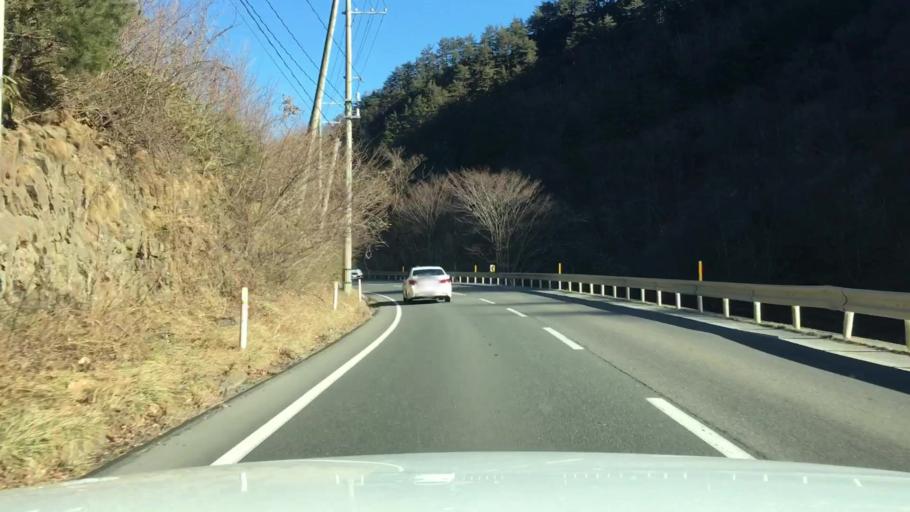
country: JP
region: Iwate
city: Miyako
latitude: 39.6094
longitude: 141.7877
